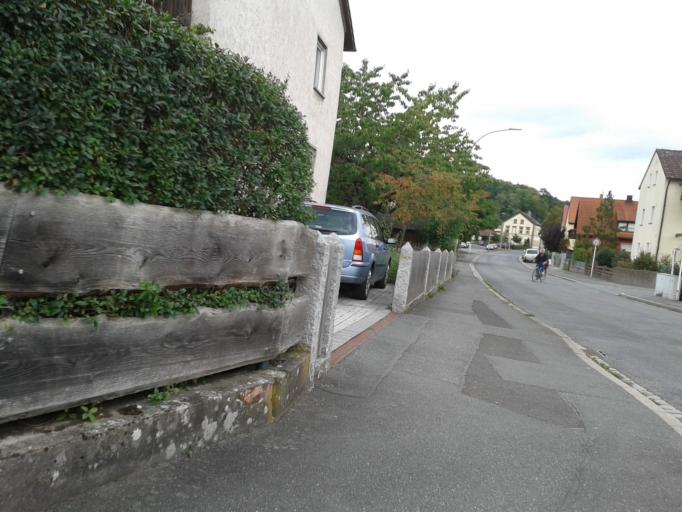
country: DE
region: Bavaria
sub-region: Upper Franconia
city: Bamberg
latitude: 49.8636
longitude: 10.9114
